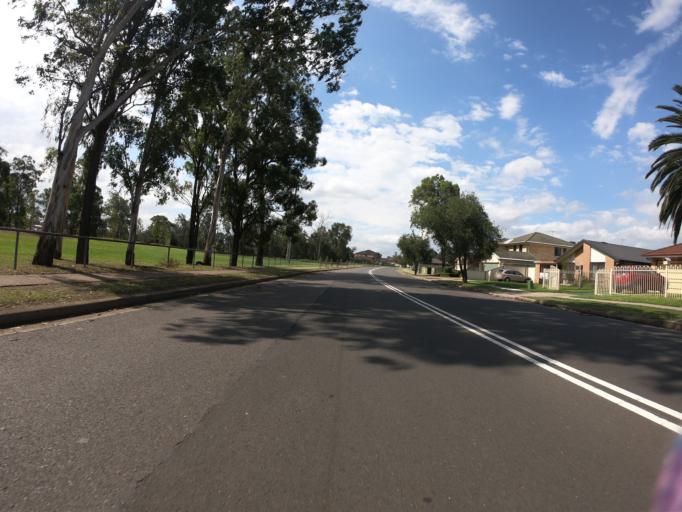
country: AU
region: New South Wales
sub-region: Blacktown
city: Hassall Grove
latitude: -33.7381
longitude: 150.8361
